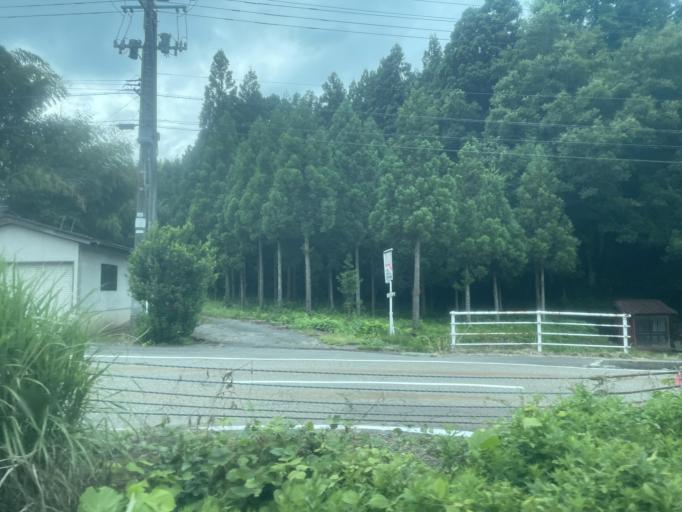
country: JP
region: Niigata
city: Nagaoka
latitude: 37.5050
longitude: 138.6986
